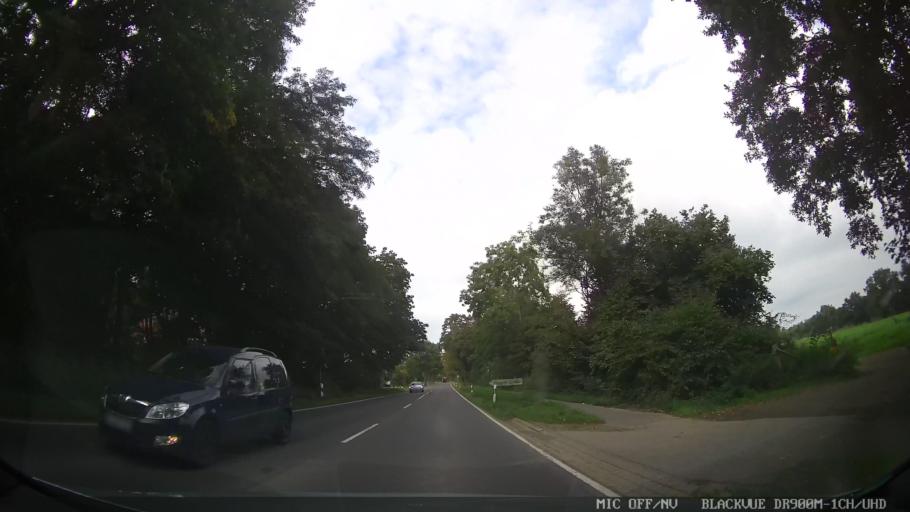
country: DE
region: Lower Saxony
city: Klein Schwulper
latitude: 52.3176
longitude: 10.4513
